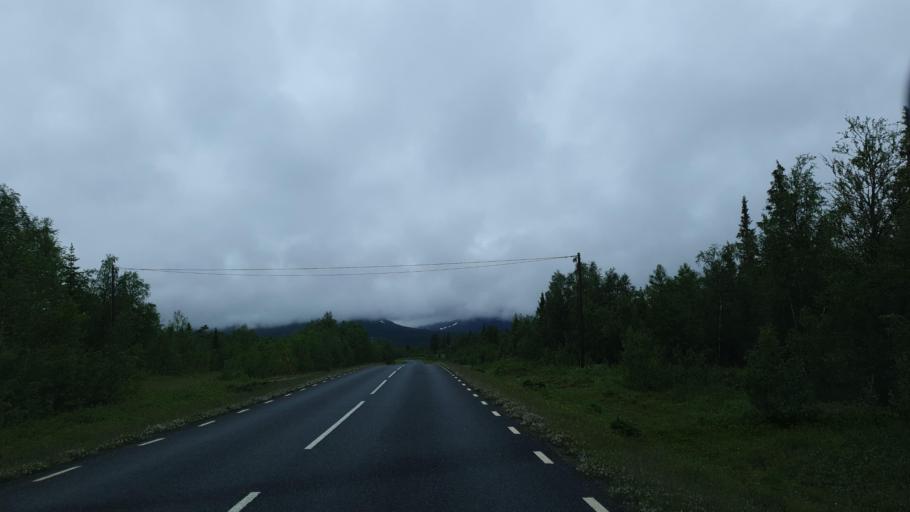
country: SE
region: Vaesterbotten
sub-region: Vilhelmina Kommun
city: Sjoberg
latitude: 65.2537
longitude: 15.7250
